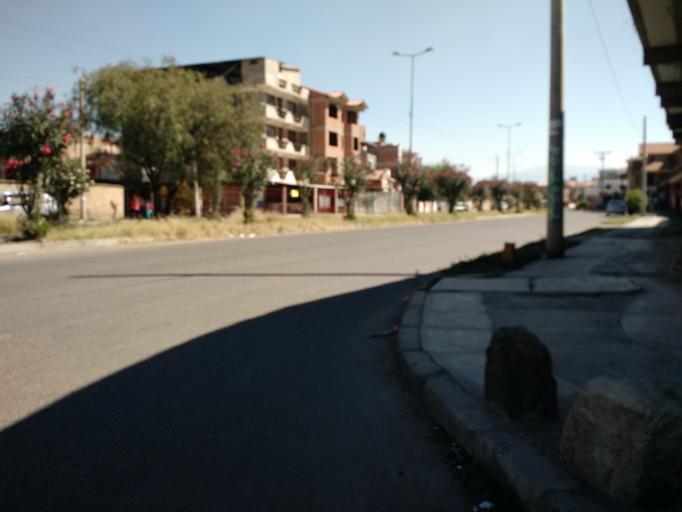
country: BO
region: Cochabamba
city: Cochabamba
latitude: -17.3859
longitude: -66.1861
